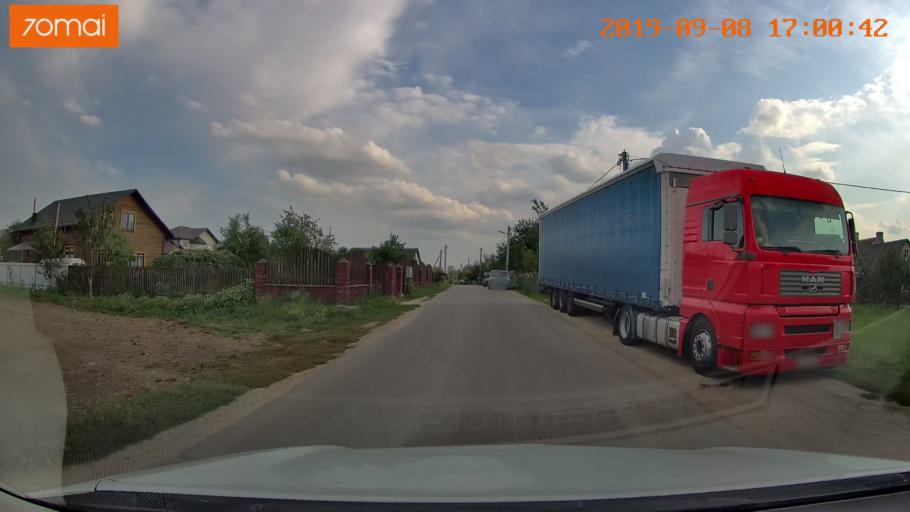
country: BY
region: Grodnenskaya
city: Hrodna
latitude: 53.7139
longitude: 23.9328
